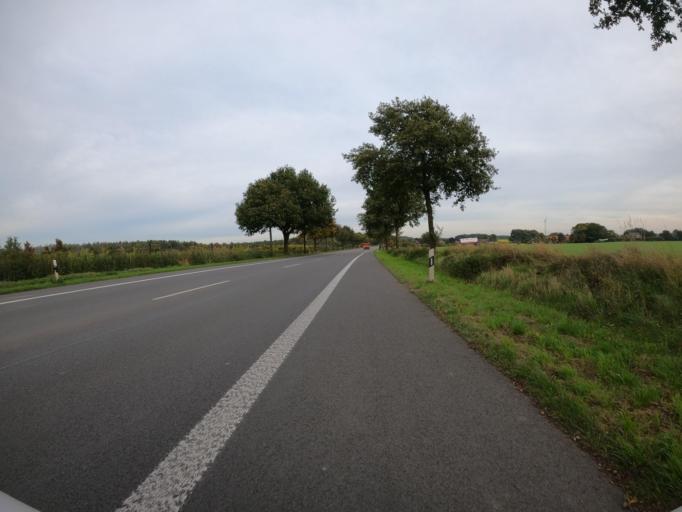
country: DE
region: North Rhine-Westphalia
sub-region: Regierungsbezirk Dusseldorf
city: Schermbeck
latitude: 51.6971
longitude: 6.8948
